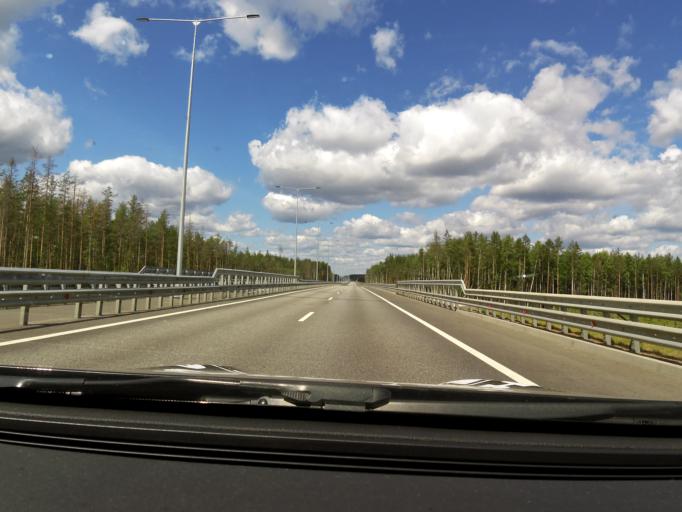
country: RU
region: Tverskaya
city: Krasnomayskiy
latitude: 57.4400
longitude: 34.4453
